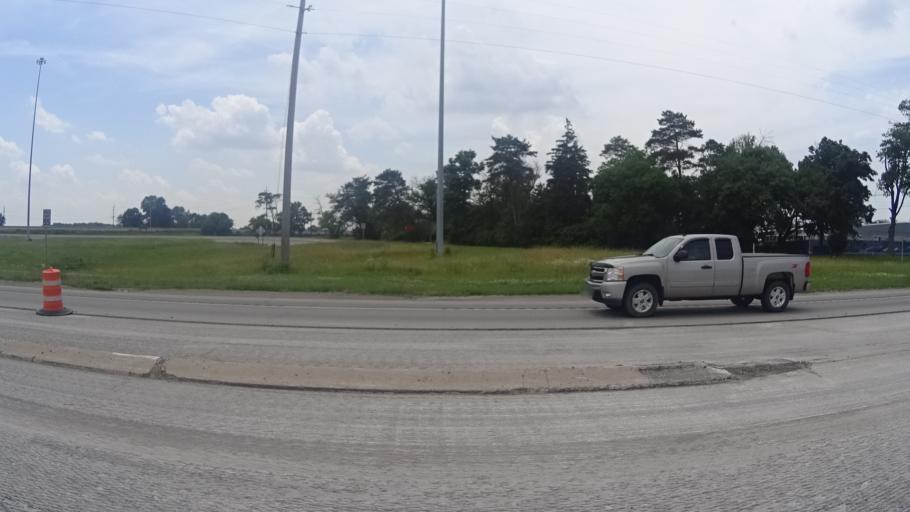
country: US
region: Ohio
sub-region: Erie County
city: Milan
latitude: 41.3254
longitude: -82.6185
